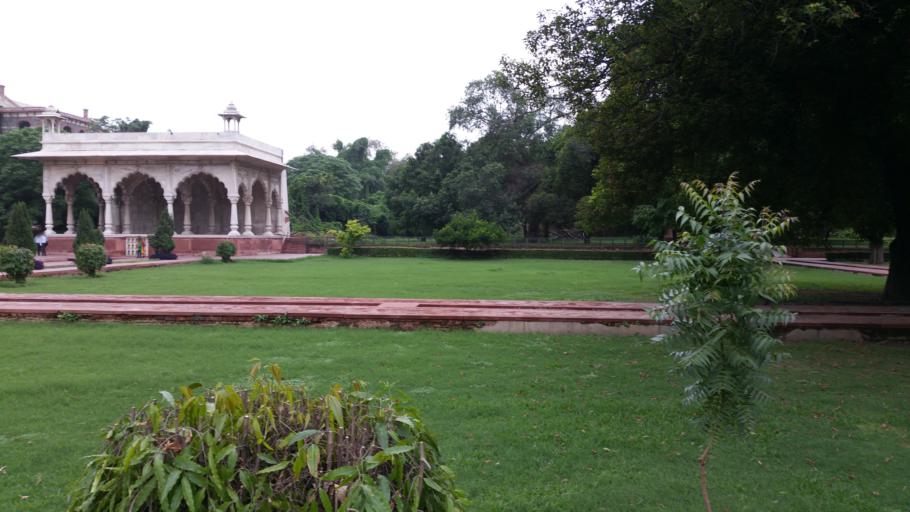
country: IN
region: NCT
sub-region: North Delhi
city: Delhi
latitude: 28.6581
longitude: 77.2430
